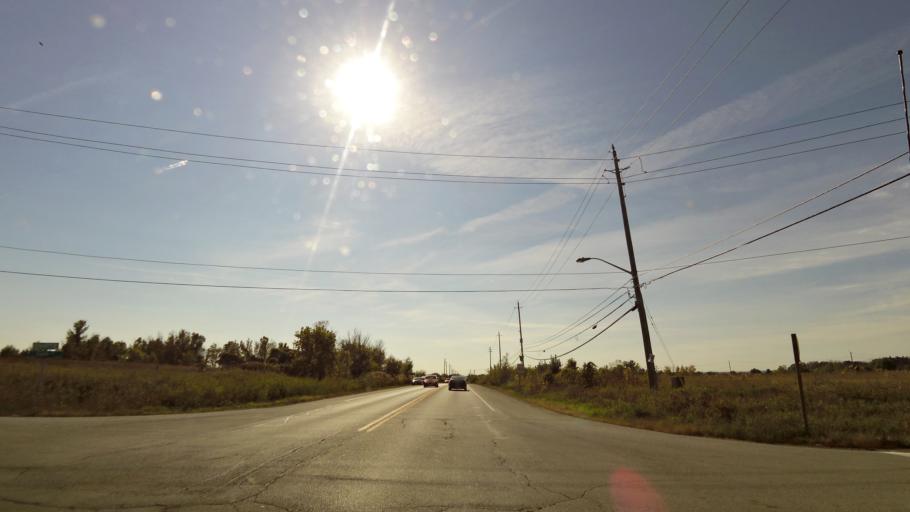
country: CA
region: Ontario
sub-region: Halton
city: Milton
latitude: 43.5453
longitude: -79.7704
